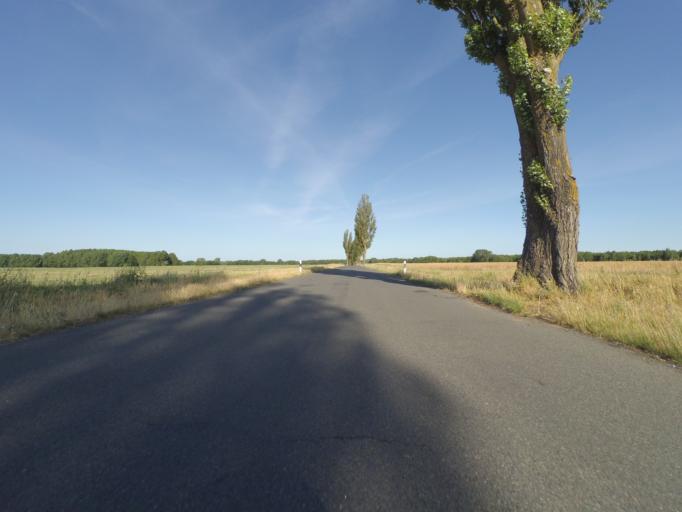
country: DE
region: Mecklenburg-Vorpommern
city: Lubz
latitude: 53.3706
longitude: 12.0835
